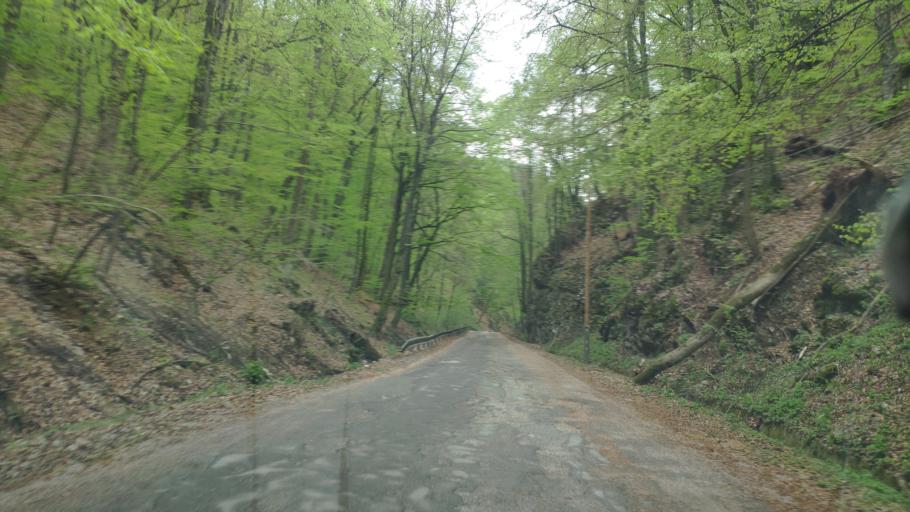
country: SK
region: Kosicky
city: Medzev
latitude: 48.6592
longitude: 20.8473
